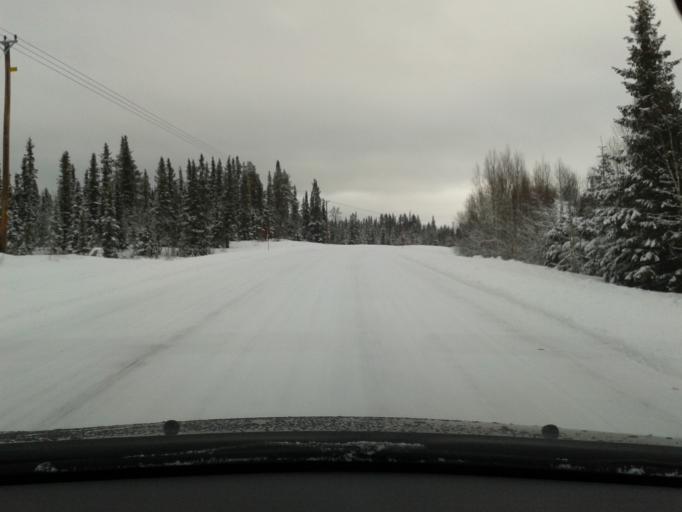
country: SE
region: Vaesterbotten
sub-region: Vilhelmina Kommun
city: Sjoberg
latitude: 65.2423
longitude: 15.7673
